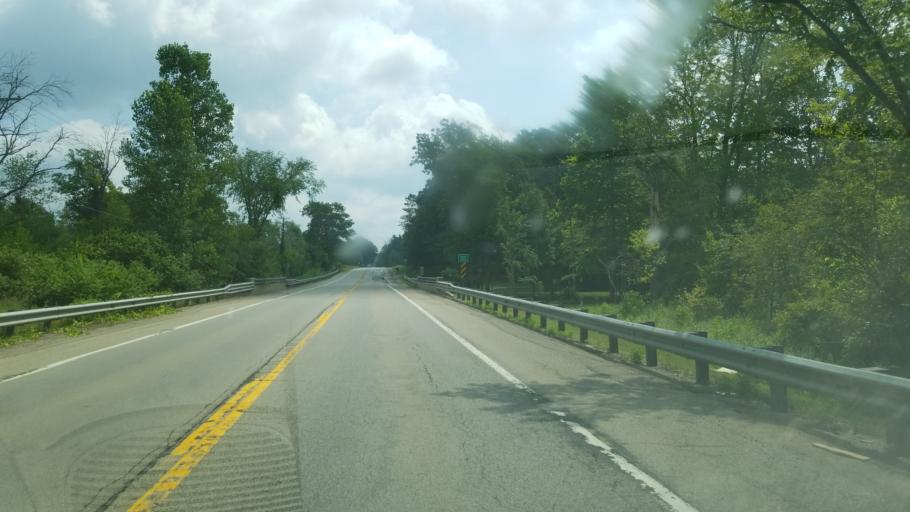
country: US
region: Michigan
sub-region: Kent County
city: Sparta
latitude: 43.2198
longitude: -85.6809
